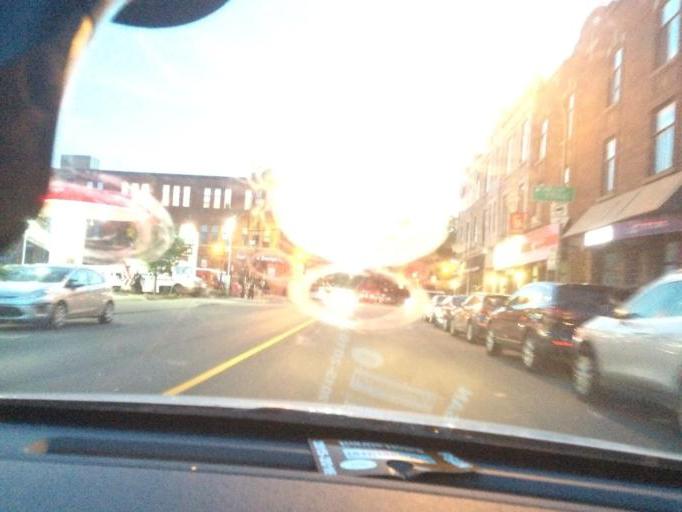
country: CA
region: Quebec
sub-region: Montreal
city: Montreal
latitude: 45.4906
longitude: -73.5668
